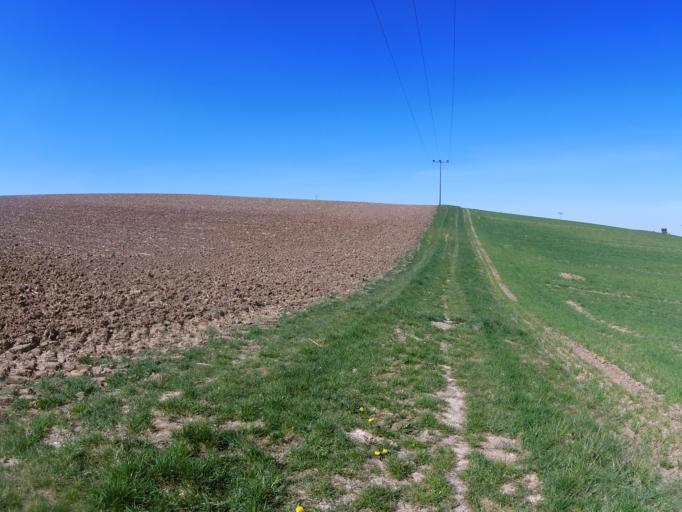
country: DE
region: Bavaria
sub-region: Regierungsbezirk Unterfranken
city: Biebelried
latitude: 49.7980
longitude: 10.0998
